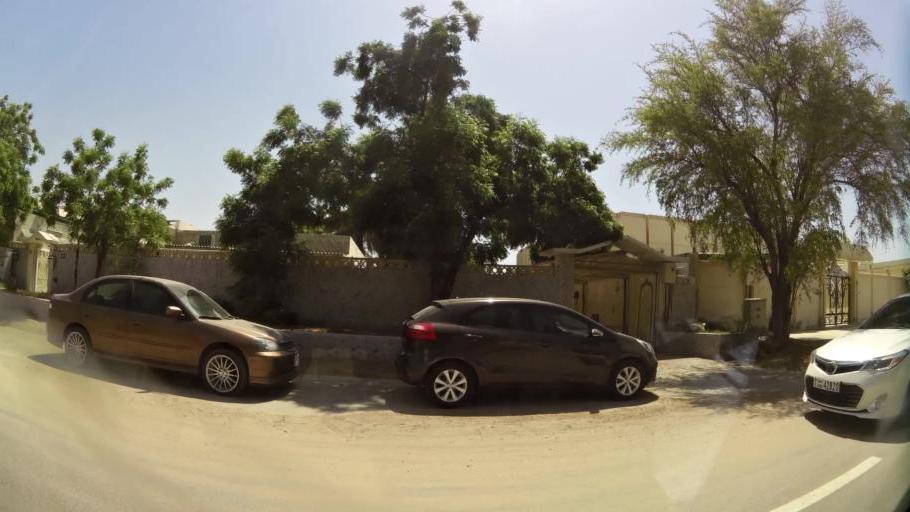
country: AE
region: Ajman
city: Ajman
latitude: 25.4187
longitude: 55.4721
